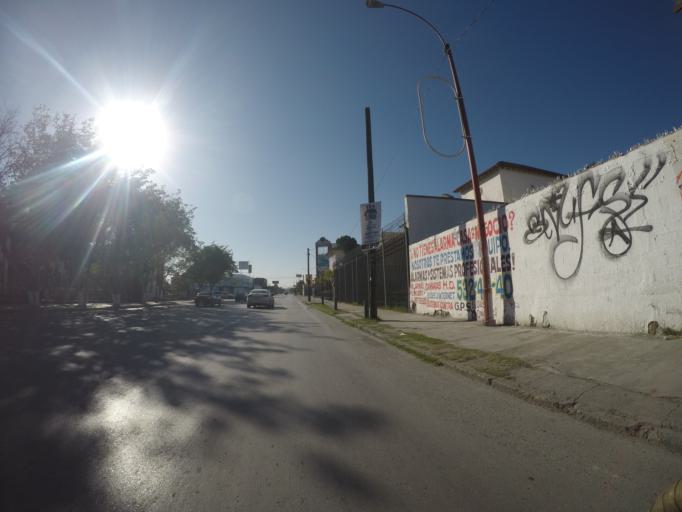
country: MX
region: Chihuahua
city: Ciudad Juarez
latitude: 31.7379
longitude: -106.4612
